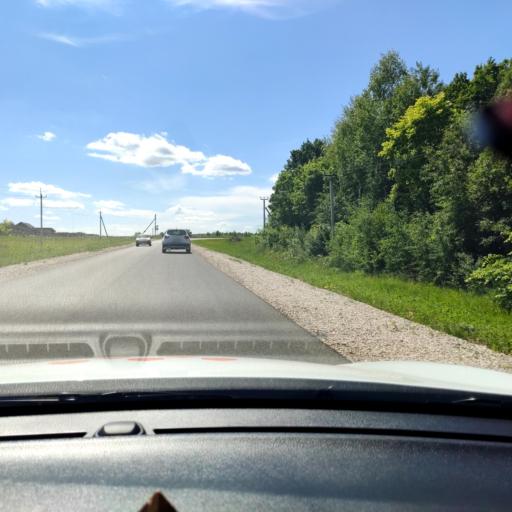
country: RU
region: Tatarstan
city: Osinovo
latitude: 55.7736
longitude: 48.8255
